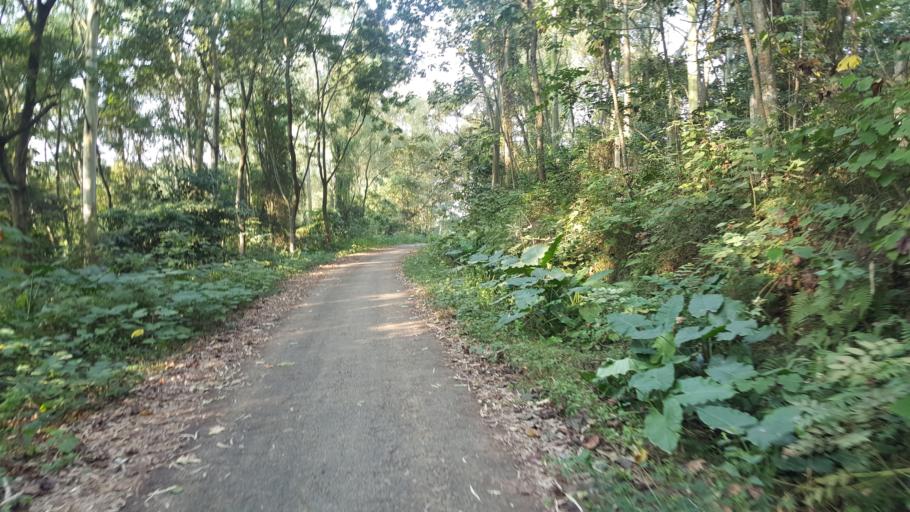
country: VN
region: Hoa Binh
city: Luong Son
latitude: 20.9144
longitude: 105.5714
